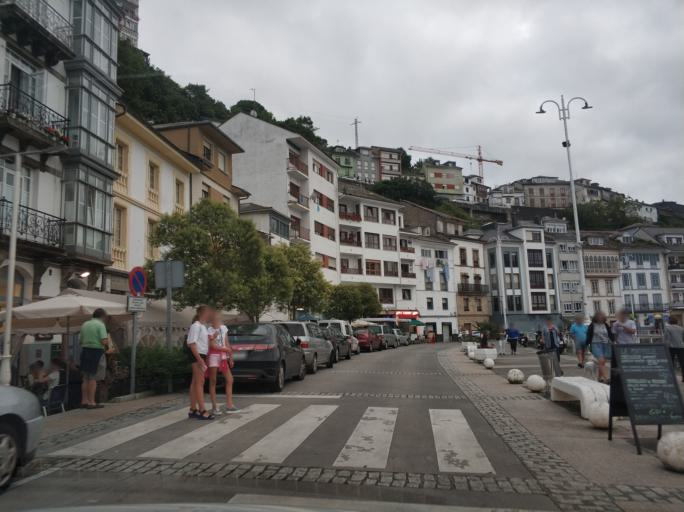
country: ES
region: Asturias
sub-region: Province of Asturias
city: Navia
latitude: 43.5459
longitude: -6.5319
